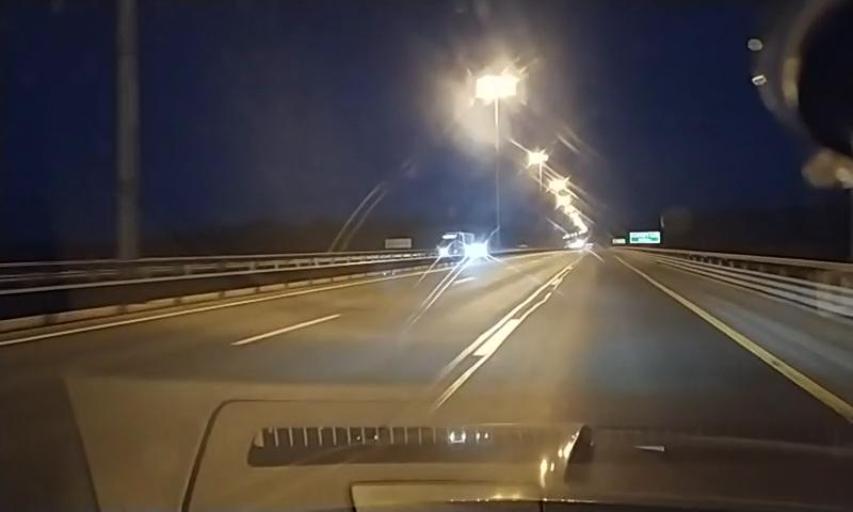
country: RU
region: St.-Petersburg
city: Pesochnyy
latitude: 60.1048
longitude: 30.0875
